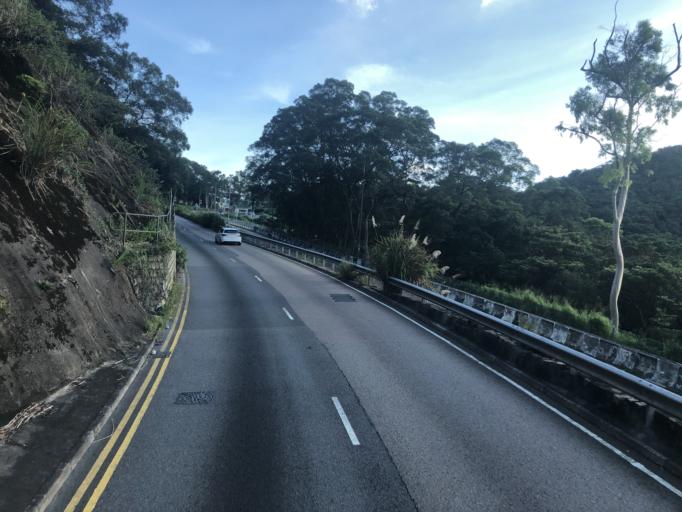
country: HK
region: Sai Kung
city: Sai Kung
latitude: 22.3426
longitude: 114.2488
